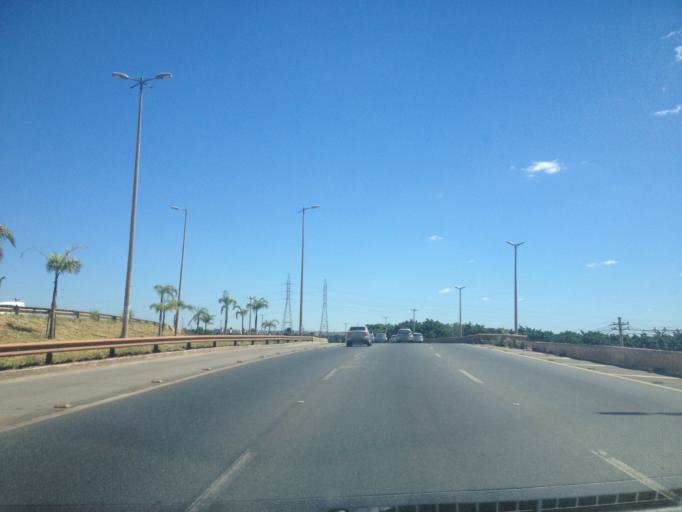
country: BR
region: Federal District
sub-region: Brasilia
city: Brasilia
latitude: -15.8072
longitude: -47.9674
